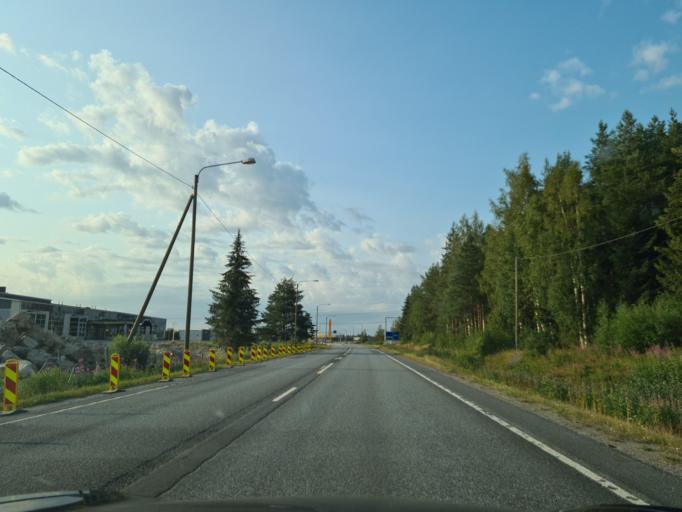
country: FI
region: Southern Ostrobothnia
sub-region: Seinaejoki
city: Kauhava
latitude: 63.0839
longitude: 23.0590
